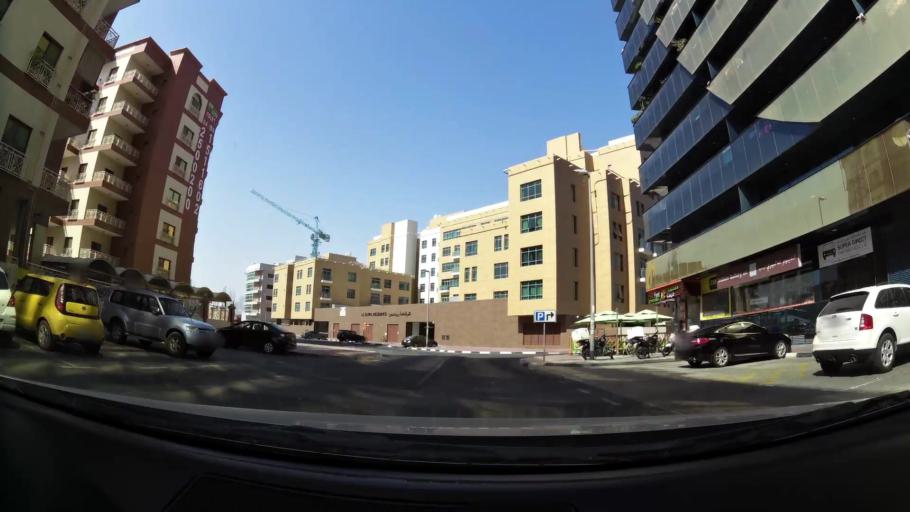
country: AE
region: Ash Shariqah
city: Sharjah
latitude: 25.2512
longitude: 55.2829
